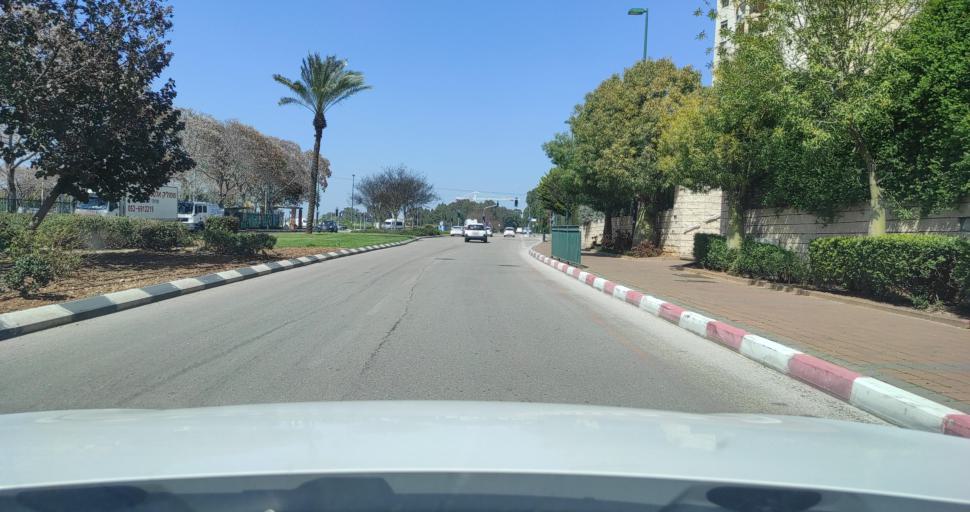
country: IL
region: Central District
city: Nordiyya
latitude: 32.3098
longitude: 34.8755
